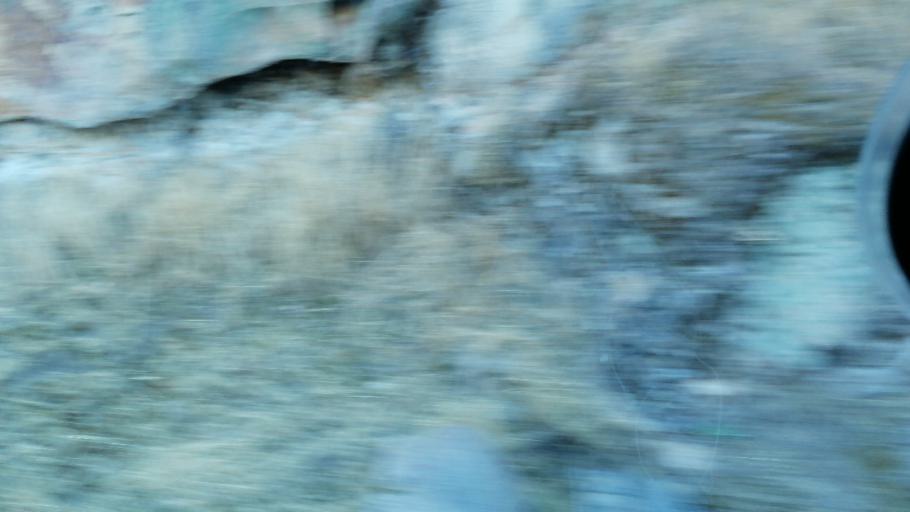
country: PT
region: Viseu
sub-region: Sao Joao da Pesqueira
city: Sao Joao da Pesqueira
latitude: 41.2245
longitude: -7.4236
